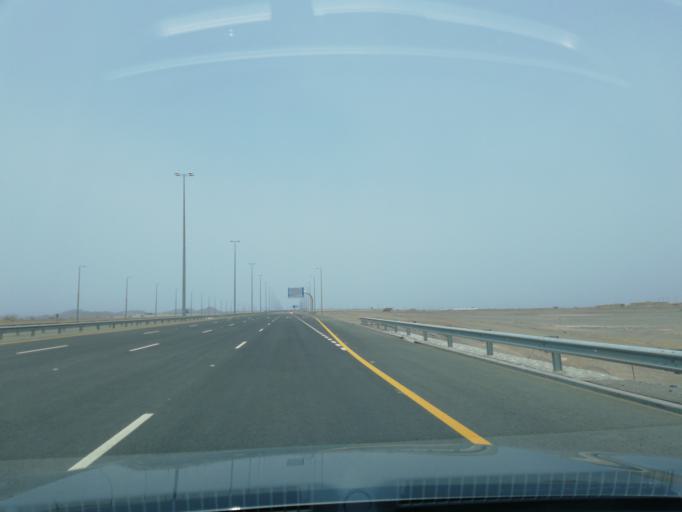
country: OM
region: Al Batinah
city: Al Liwa'
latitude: 24.4415
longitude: 56.5218
